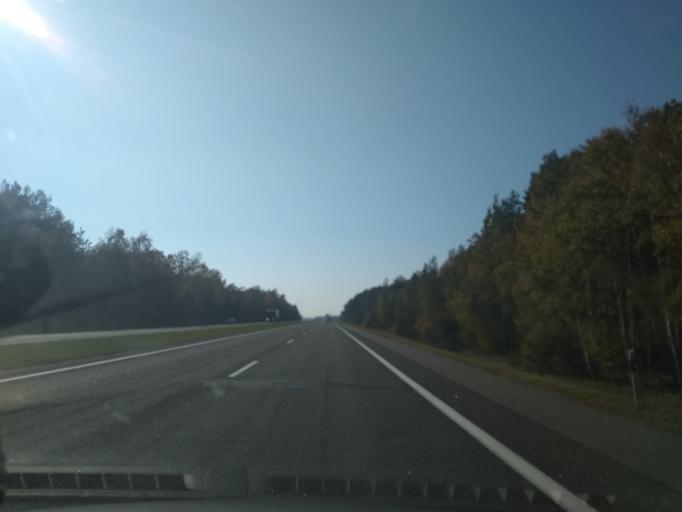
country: BY
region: Brest
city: Antopal'
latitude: 52.3402
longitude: 24.6503
